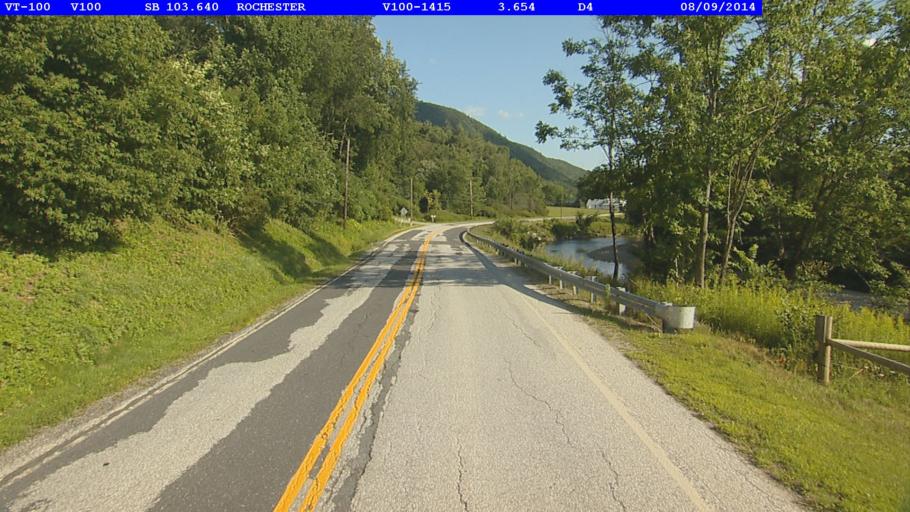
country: US
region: Vermont
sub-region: Orange County
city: Randolph
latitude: 43.8541
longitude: -72.8021
